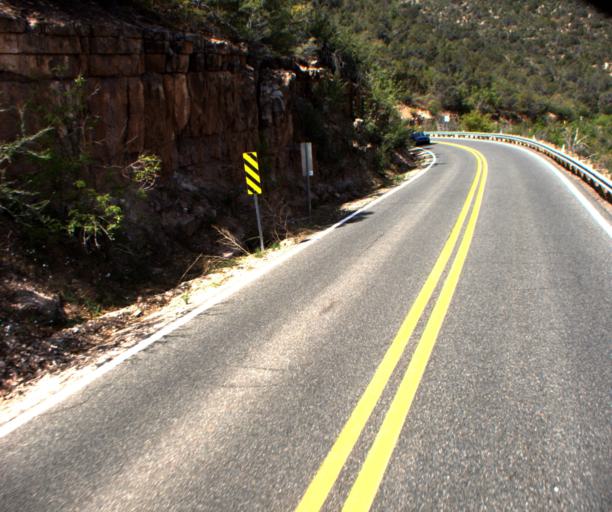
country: US
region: Arizona
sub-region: Yavapai County
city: Clarkdale
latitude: 34.7391
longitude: -112.1393
